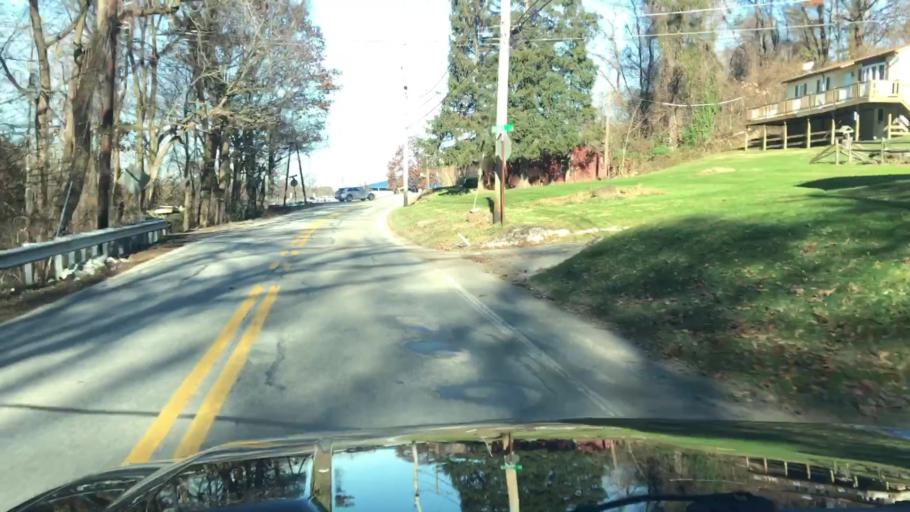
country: US
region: Pennsylvania
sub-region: Cumberland County
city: Lower Allen
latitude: 40.1878
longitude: -76.8888
